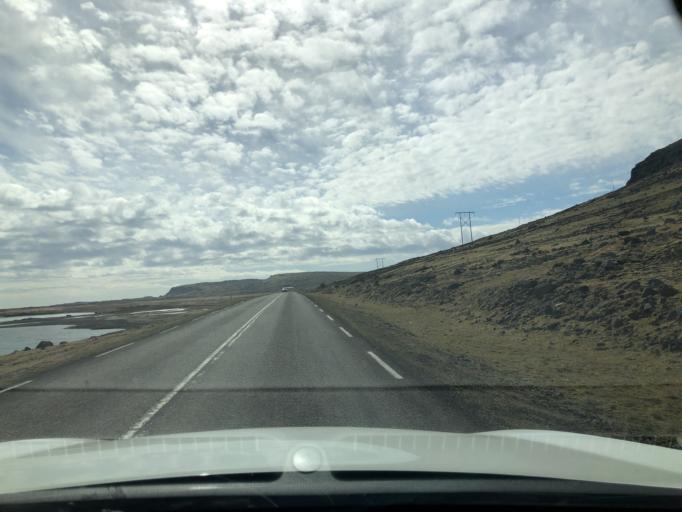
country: IS
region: East
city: Reydarfjoerdur
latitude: 64.7003
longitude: -14.3877
